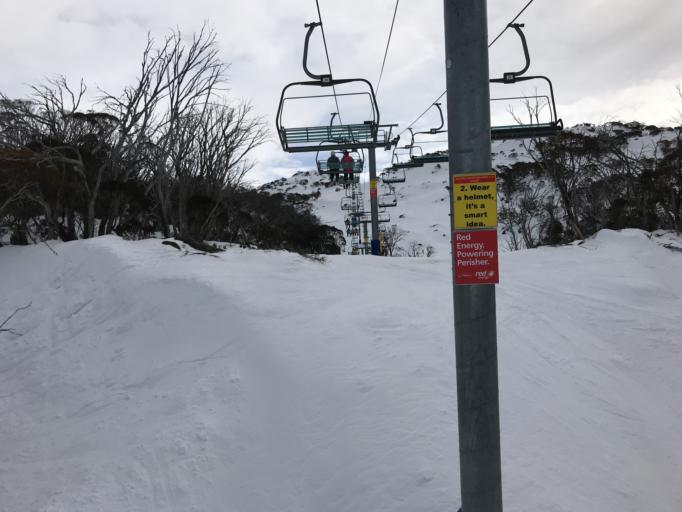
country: AU
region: New South Wales
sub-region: Snowy River
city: Jindabyne
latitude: -36.3942
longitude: 148.4074
